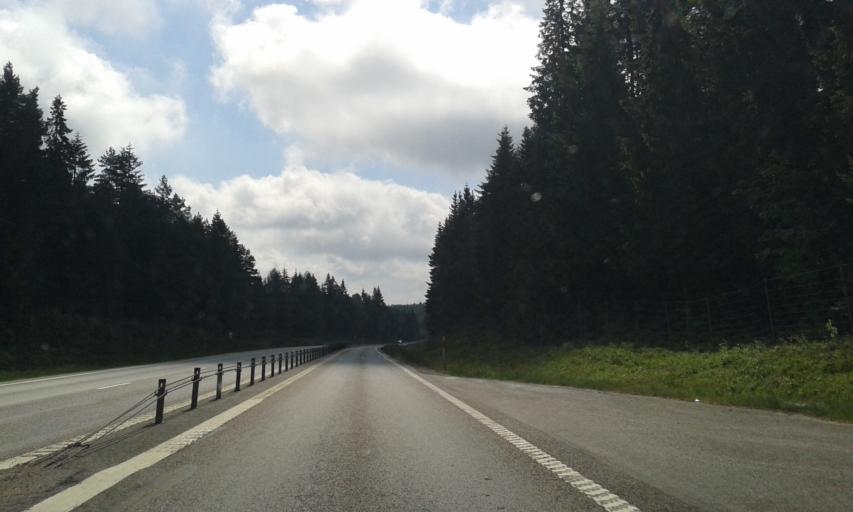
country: SE
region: Vaestra Goetaland
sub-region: Boras Kommun
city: Dalsjofors
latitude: 57.6268
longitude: 13.0942
